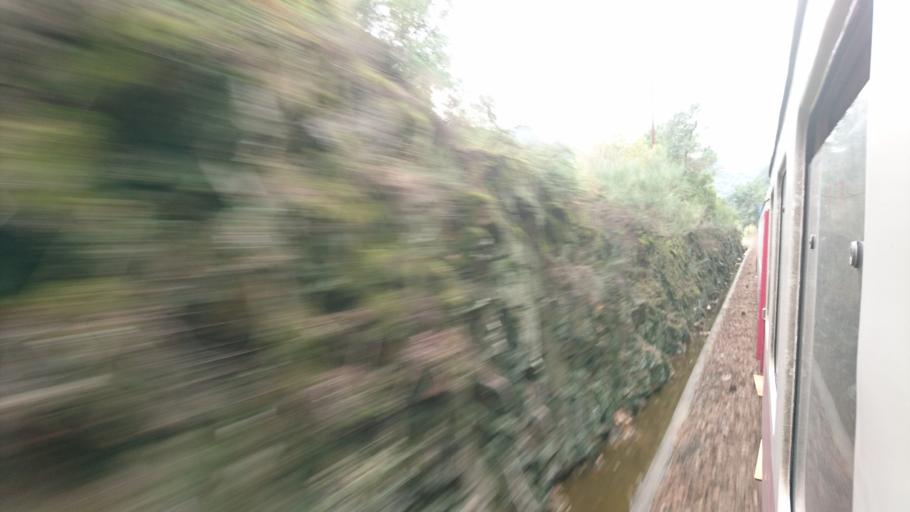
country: PT
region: Viseu
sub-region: Cinfaes
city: Cinfaes
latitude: 41.0964
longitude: -8.0393
